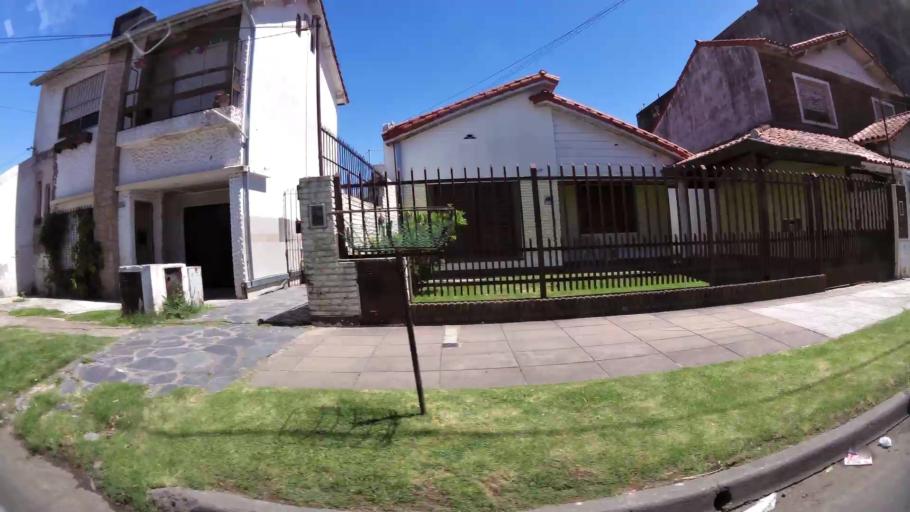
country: AR
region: Buenos Aires
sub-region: Partido de San Isidro
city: San Isidro
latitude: -34.5059
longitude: -58.5697
